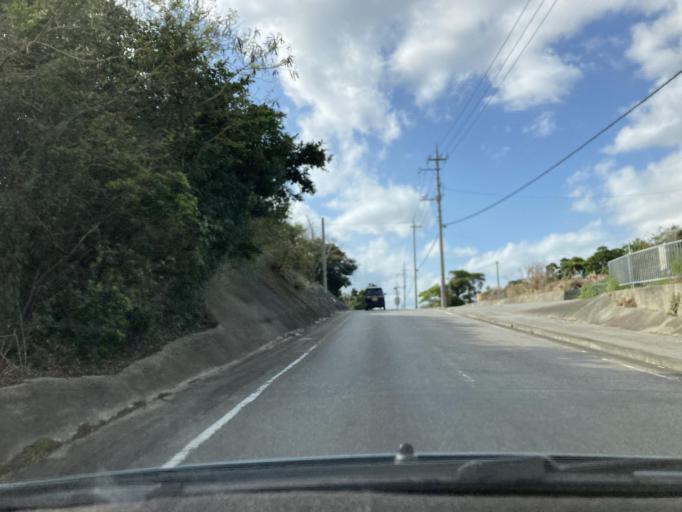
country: JP
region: Okinawa
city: Tomigusuku
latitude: 26.1702
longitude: 127.7631
